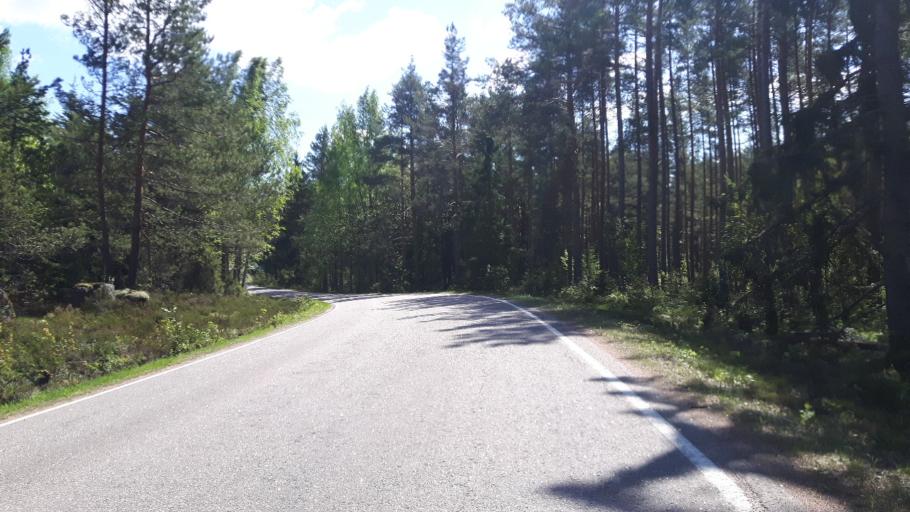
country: FI
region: Kymenlaakso
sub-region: Kotka-Hamina
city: Hamina
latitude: 60.5122
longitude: 27.3954
